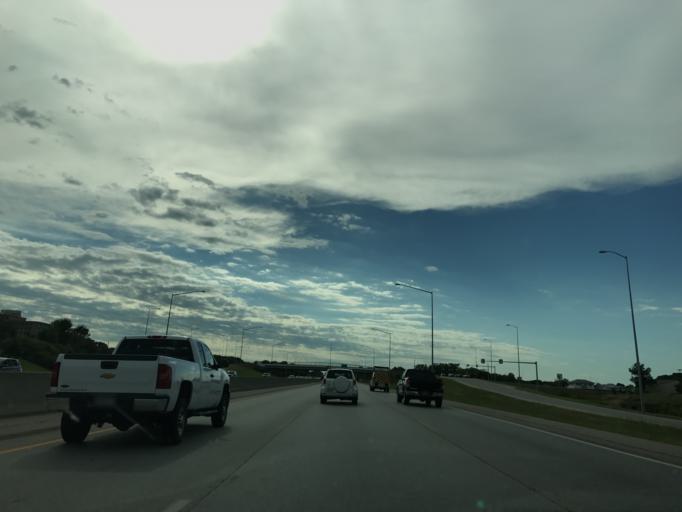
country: US
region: Iowa
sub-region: Polk County
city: Clive
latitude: 41.5924
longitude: -93.7470
